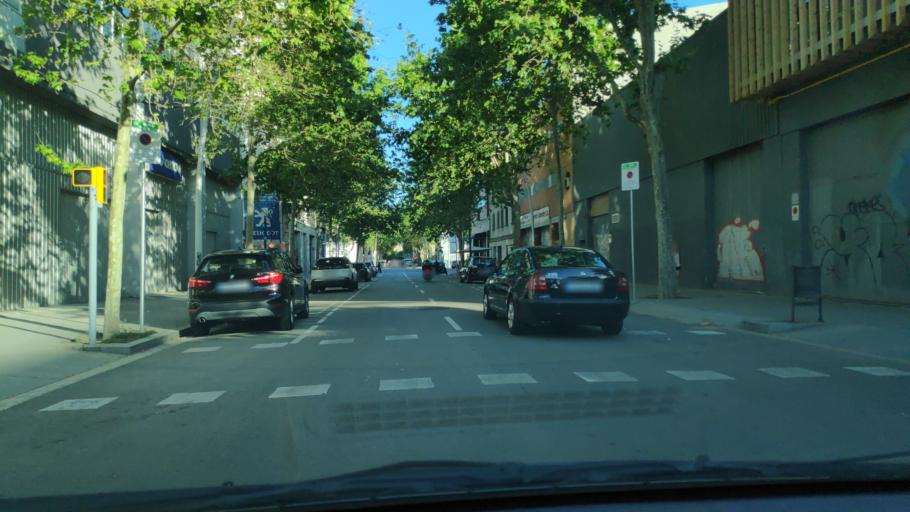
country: ES
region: Catalonia
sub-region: Provincia de Barcelona
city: Sant Marti
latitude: 41.3998
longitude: 2.1917
